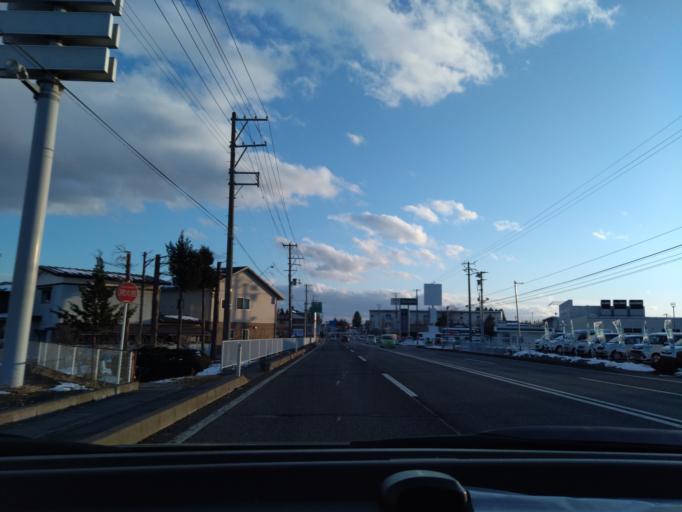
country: JP
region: Iwate
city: Morioka-shi
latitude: 39.5441
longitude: 141.1688
